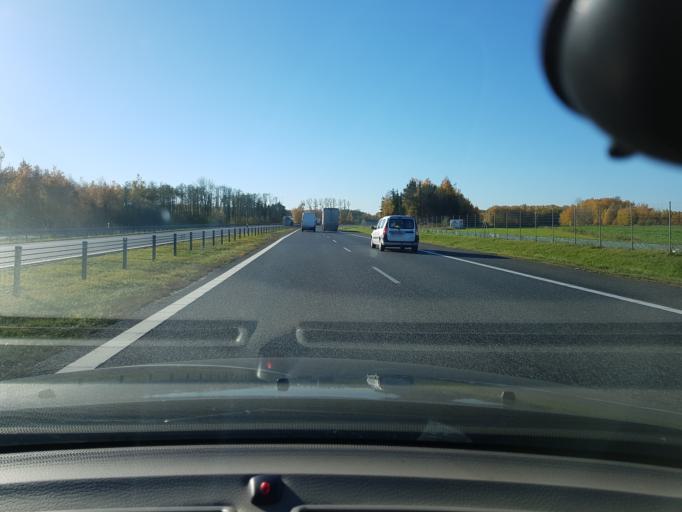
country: PL
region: Masovian Voivodeship
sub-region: Powiat zyrardowski
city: Mszczonow
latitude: 51.9616
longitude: 20.4990
